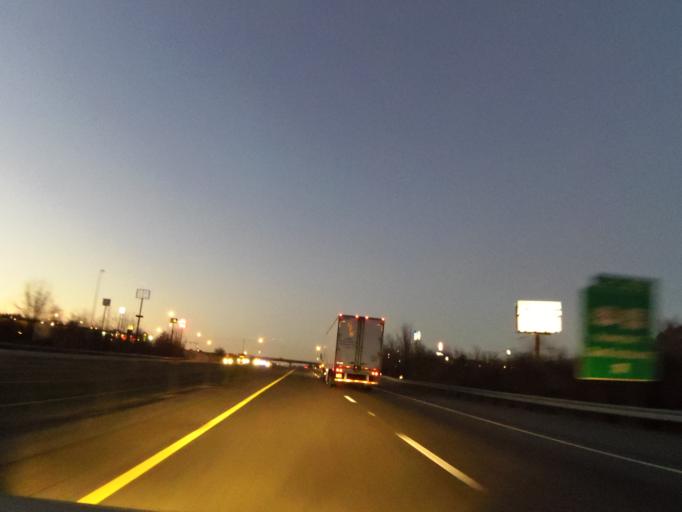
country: US
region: Tennessee
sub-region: Cocke County
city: Newport
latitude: 35.9442
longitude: -83.2015
